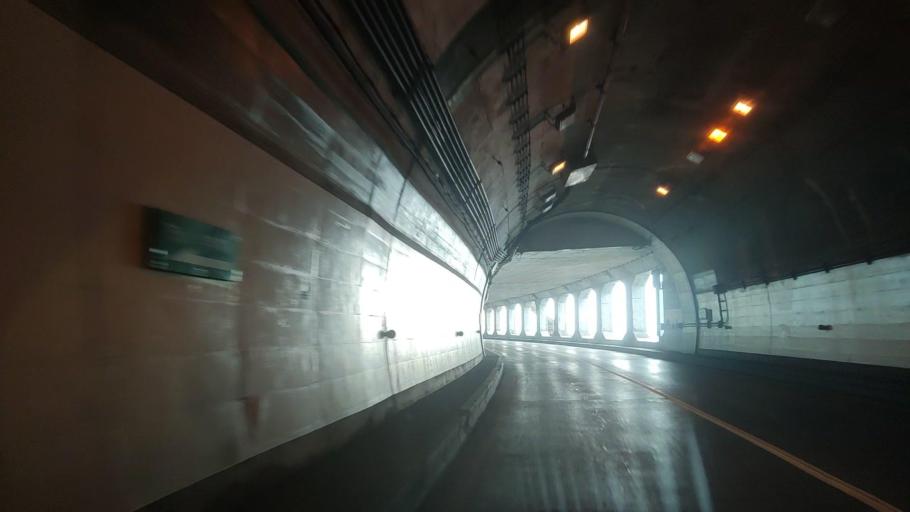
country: JP
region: Hokkaido
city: Rumoi
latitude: 43.8016
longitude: 141.3827
